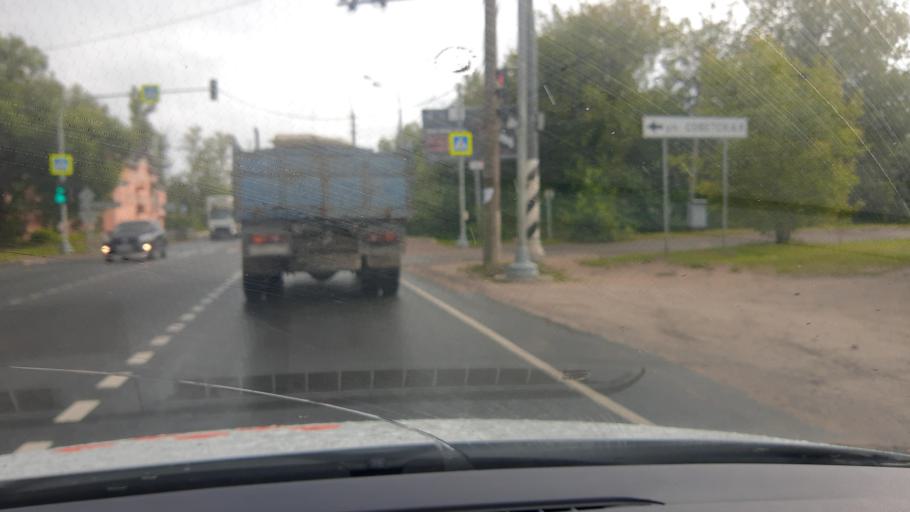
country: RU
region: Moskovskaya
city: Elektrostal'
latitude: 55.7900
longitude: 38.4306
